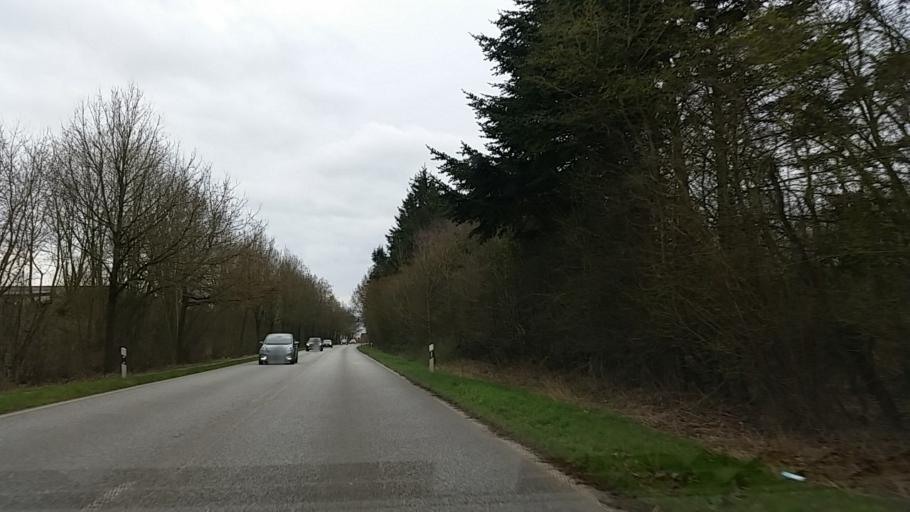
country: DE
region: Schleswig-Holstein
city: Braak
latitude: 53.6136
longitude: 10.2411
